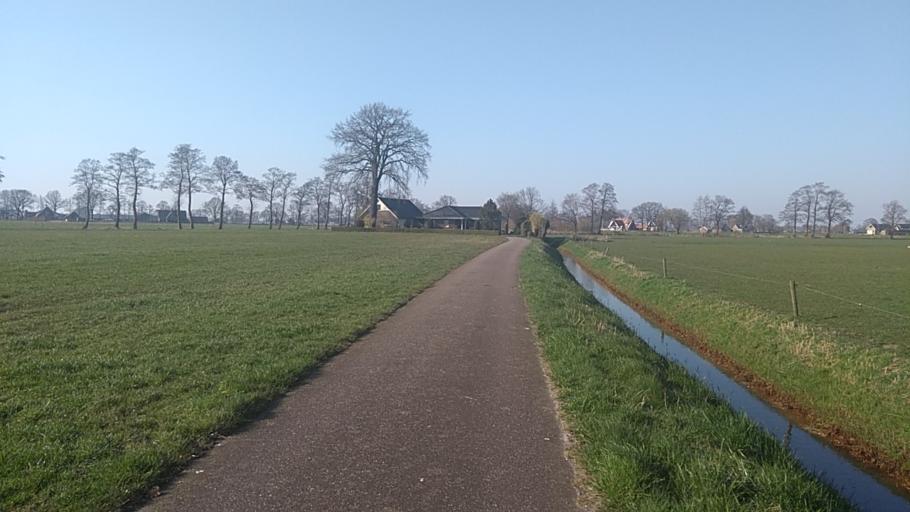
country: NL
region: Overijssel
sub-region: Gemeente Almelo
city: Almelo
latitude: 52.3864
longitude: 6.7006
